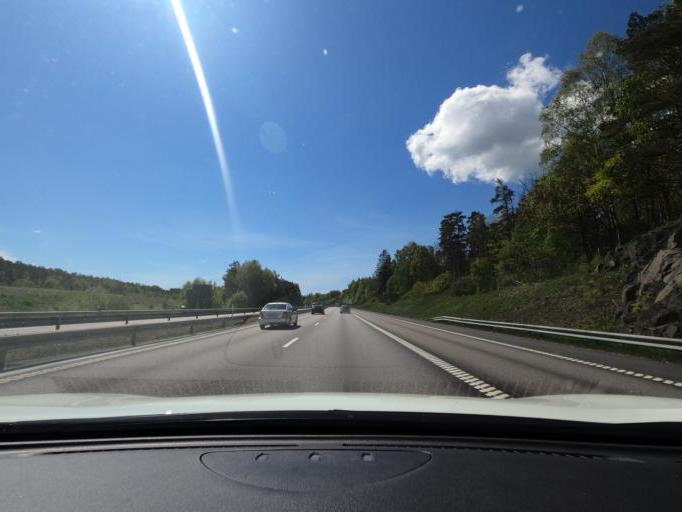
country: SE
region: Halland
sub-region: Kungsbacka Kommun
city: Kungsbacka
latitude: 57.4858
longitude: 12.0443
